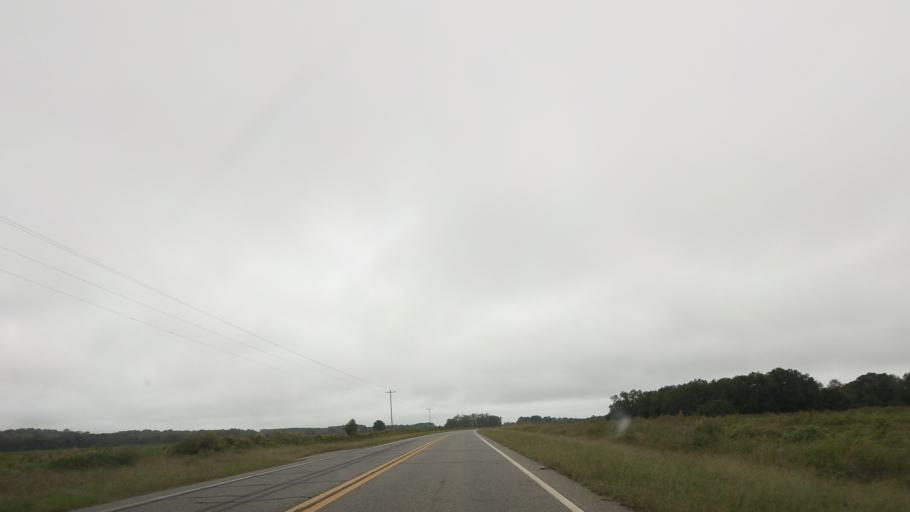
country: US
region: Georgia
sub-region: Irwin County
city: Ocilla
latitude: 31.5193
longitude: -83.2430
